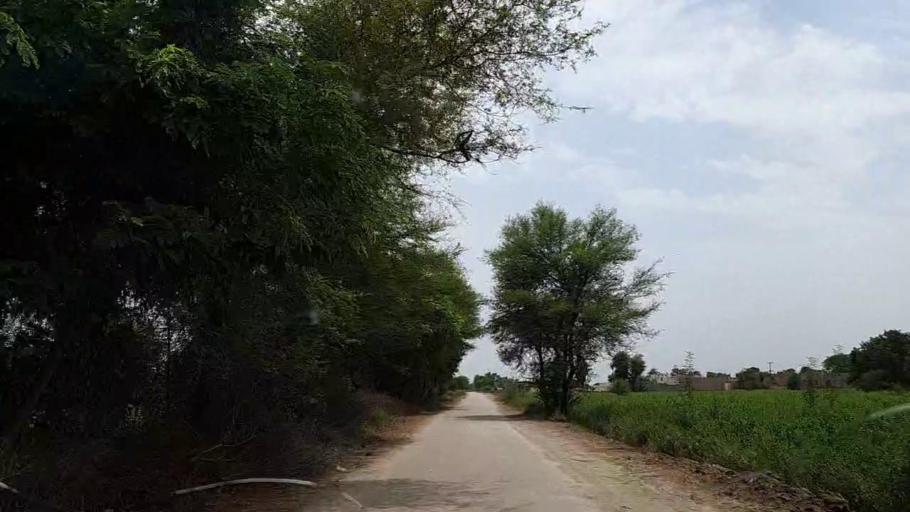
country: PK
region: Sindh
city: Tharu Shah
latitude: 26.9299
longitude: 68.1046
